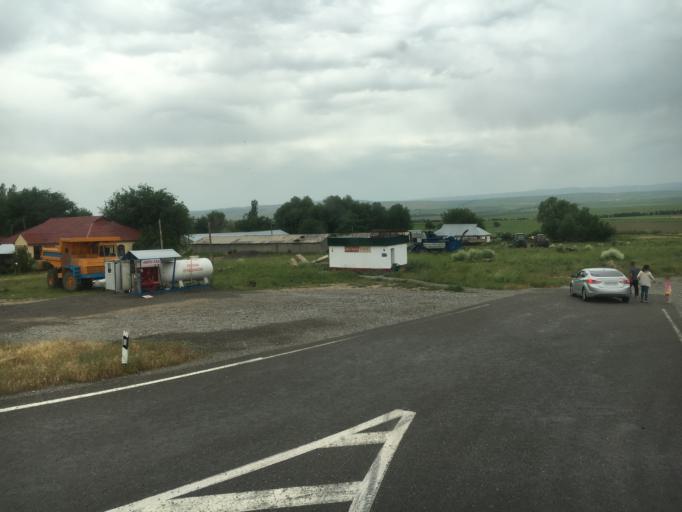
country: KZ
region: Ongtustik Qazaqstan
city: Sastobe
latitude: 42.5502
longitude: 70.0986
